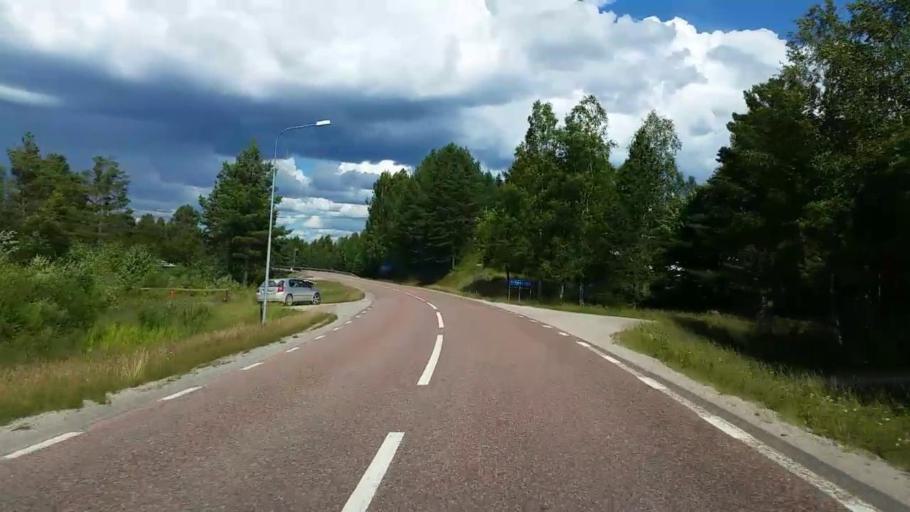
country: SE
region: Gaevleborg
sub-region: Ovanakers Kommun
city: Edsbyn
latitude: 61.3341
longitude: 15.5409
